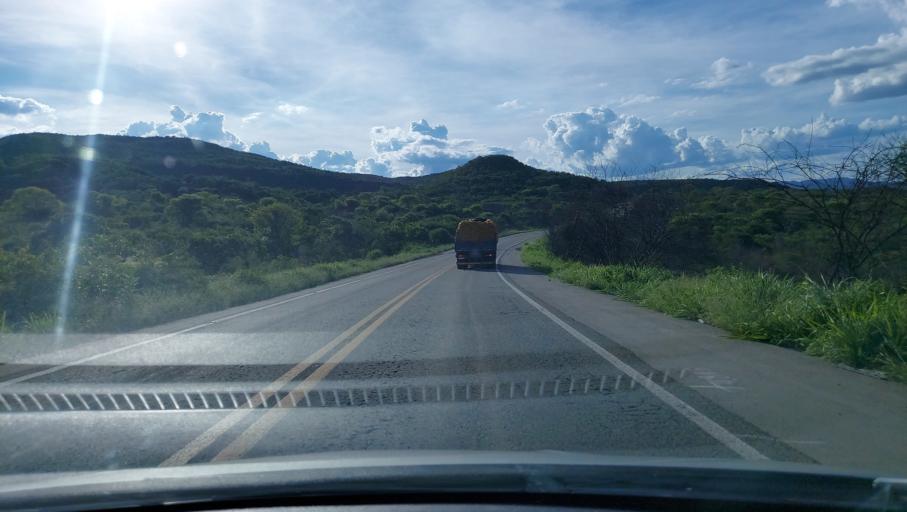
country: BR
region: Bahia
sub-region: Seabra
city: Seabra
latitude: -12.4523
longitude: -42.1584
